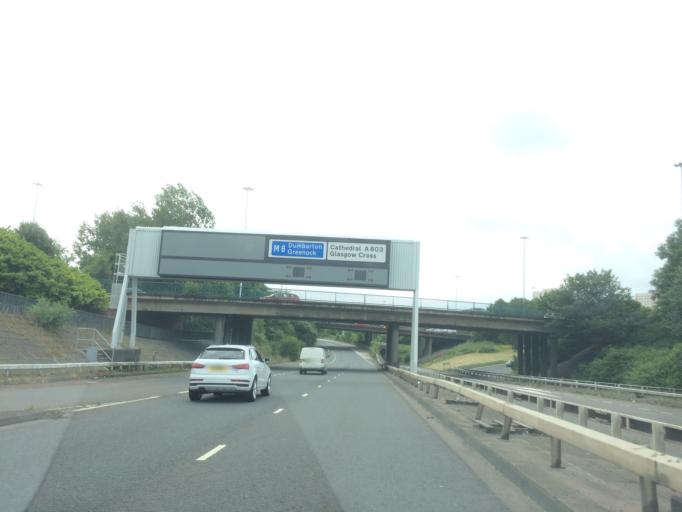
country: GB
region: Scotland
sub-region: Glasgow City
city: Glasgow
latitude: 55.8694
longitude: -4.2346
